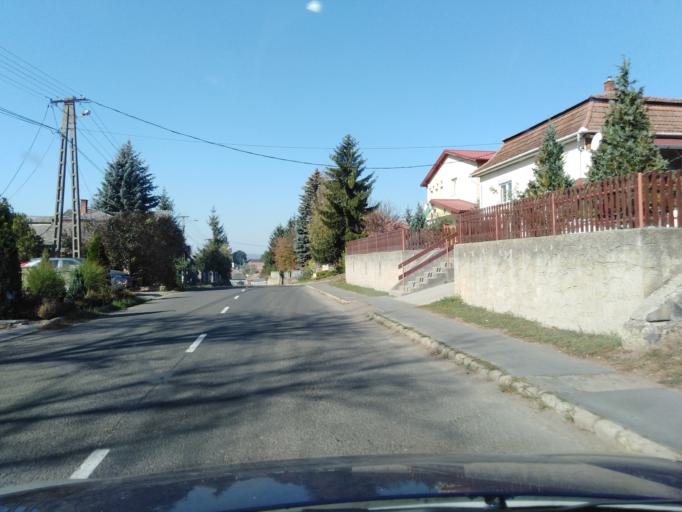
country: HU
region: Nograd
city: Karancskeszi
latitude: 48.1617
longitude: 19.7061
